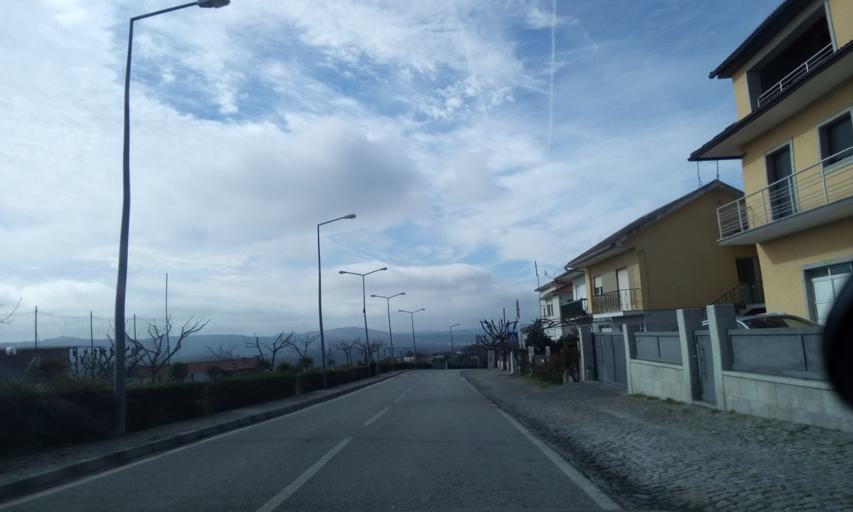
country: PT
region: Guarda
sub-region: Aguiar da Beira
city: Aguiar da Beira
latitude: 40.7379
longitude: -7.5552
